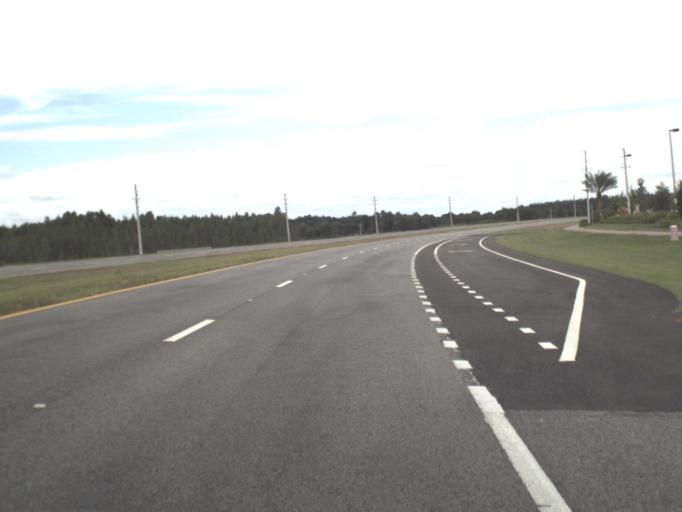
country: US
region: Florida
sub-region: Pasco County
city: Wesley Chapel
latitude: 28.2014
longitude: -82.3249
